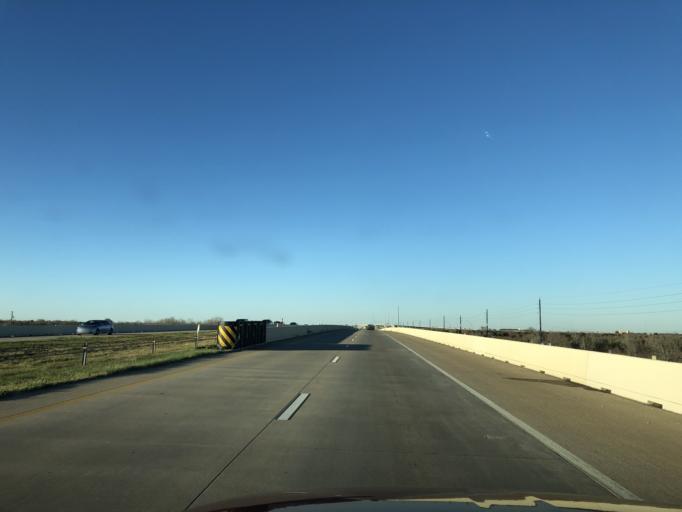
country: US
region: Texas
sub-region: Harris County
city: Cypress
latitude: 29.9765
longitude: -95.7694
